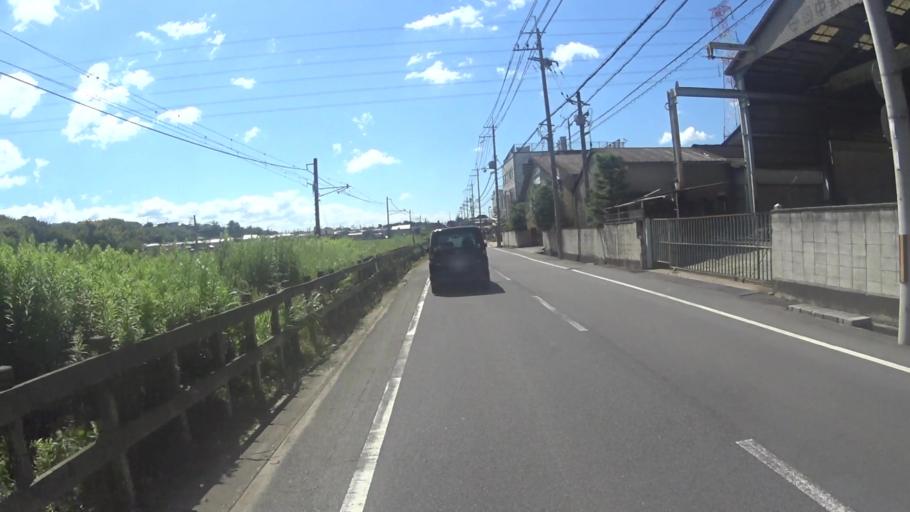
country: JP
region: Kyoto
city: Tanabe
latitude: 34.8061
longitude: 135.8067
